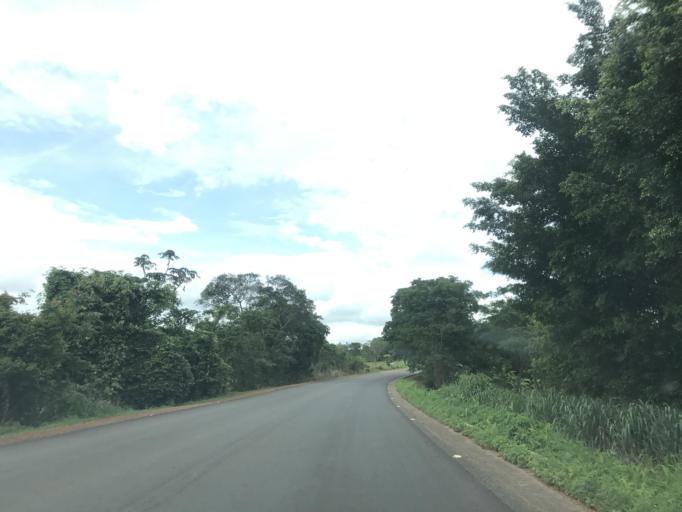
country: BR
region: Goias
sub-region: Bela Vista De Goias
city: Bela Vista de Goias
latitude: -17.0381
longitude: -48.6621
